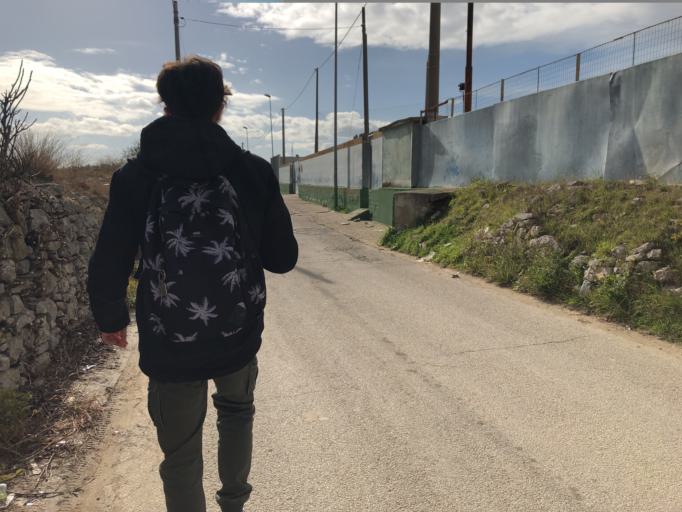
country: IT
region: Apulia
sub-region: Provincia di Barletta - Andria - Trani
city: Andria
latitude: 41.2172
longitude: 16.3055
